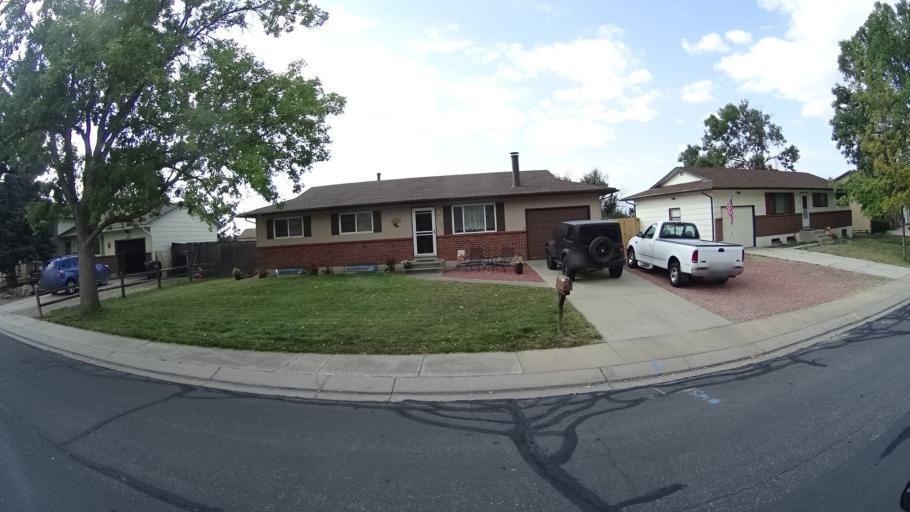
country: US
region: Colorado
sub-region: El Paso County
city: Cimarron Hills
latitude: 38.8823
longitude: -104.7400
